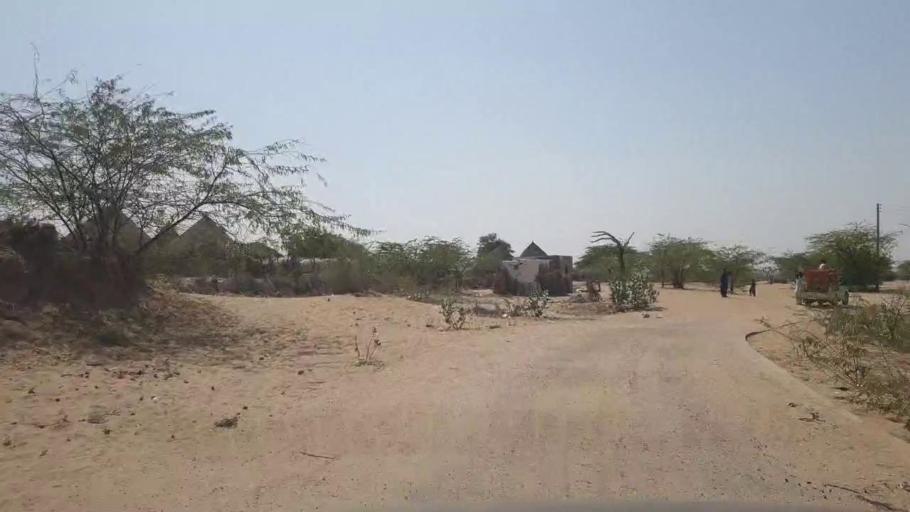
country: PK
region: Sindh
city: Chor
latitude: 25.5633
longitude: 70.1798
